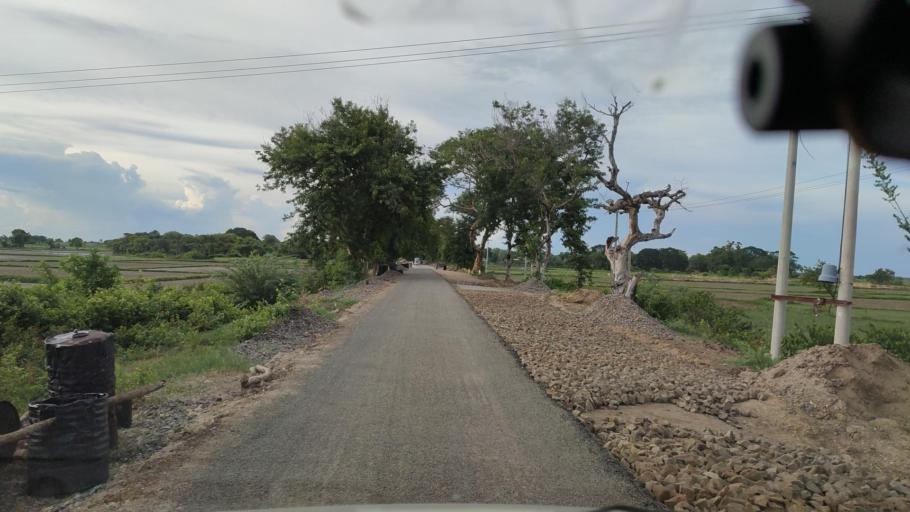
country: MM
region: Magway
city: Minbu
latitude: 20.3138
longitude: 94.7576
